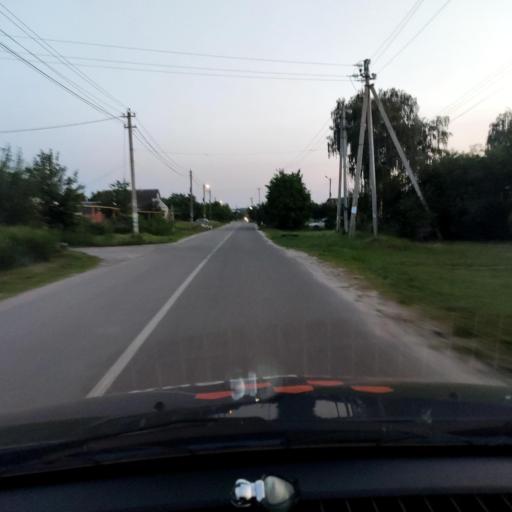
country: RU
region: Voronezj
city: Ramon'
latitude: 51.8138
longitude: 39.2629
